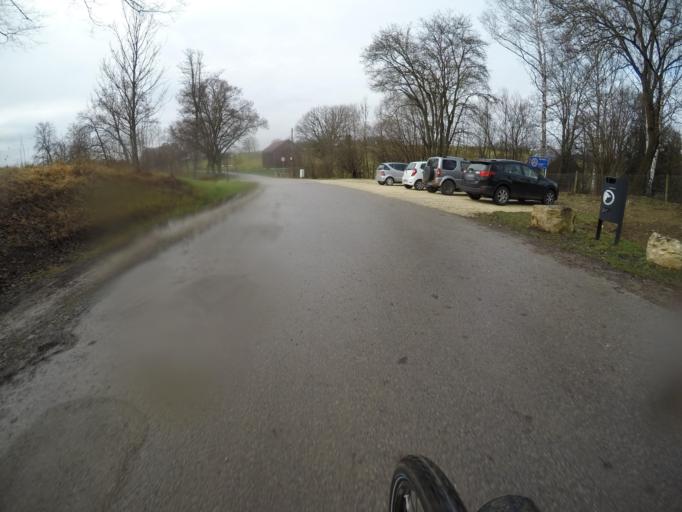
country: DE
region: Baden-Wuerttemberg
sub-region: Regierungsbezirk Stuttgart
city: Frickenhausen
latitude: 48.6135
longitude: 9.3773
